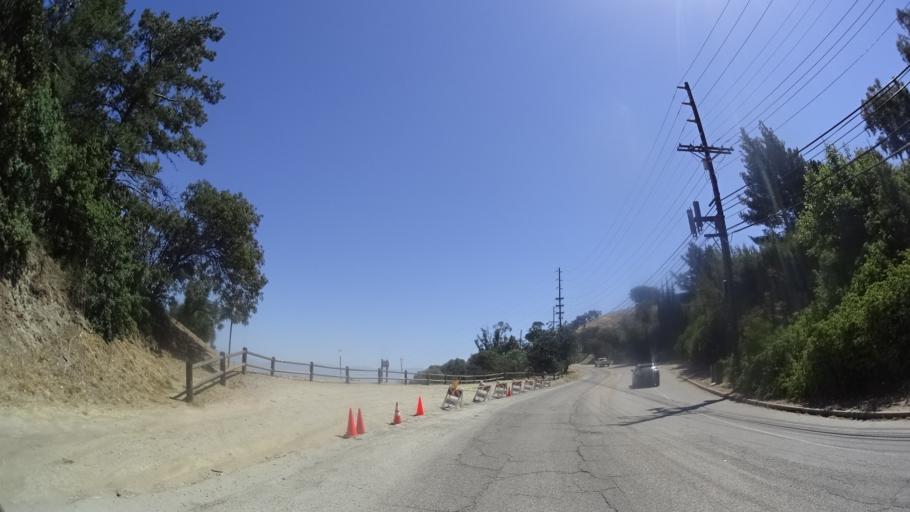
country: US
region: California
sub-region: Los Angeles County
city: Sherman Oaks
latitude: 34.1321
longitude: -118.4572
